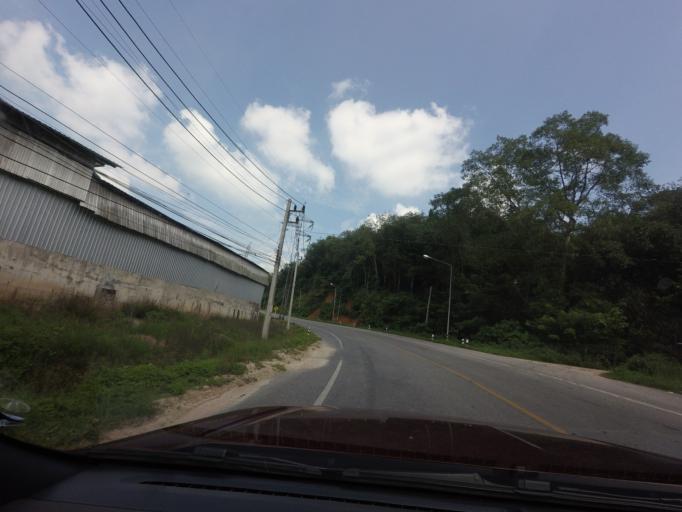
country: TH
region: Yala
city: Betong
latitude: 5.8229
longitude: 101.1050
